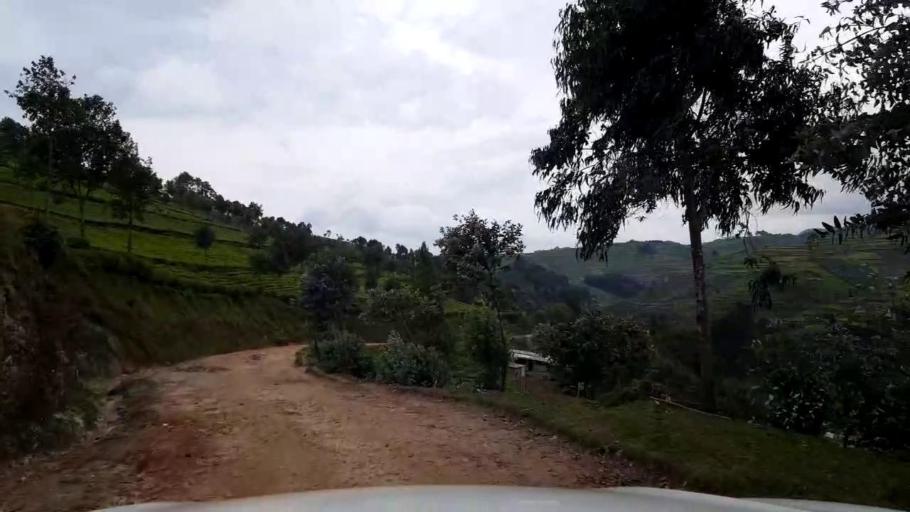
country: RW
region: Western Province
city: Kibuye
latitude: -1.9565
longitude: 29.4235
